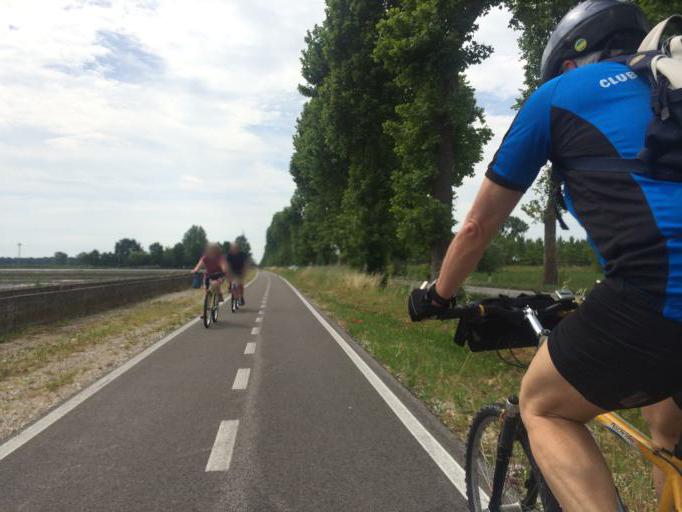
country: IT
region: Friuli Venezia Giulia
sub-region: Provincia di Udine
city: Aquileia
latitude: 45.7508
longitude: 13.3790
